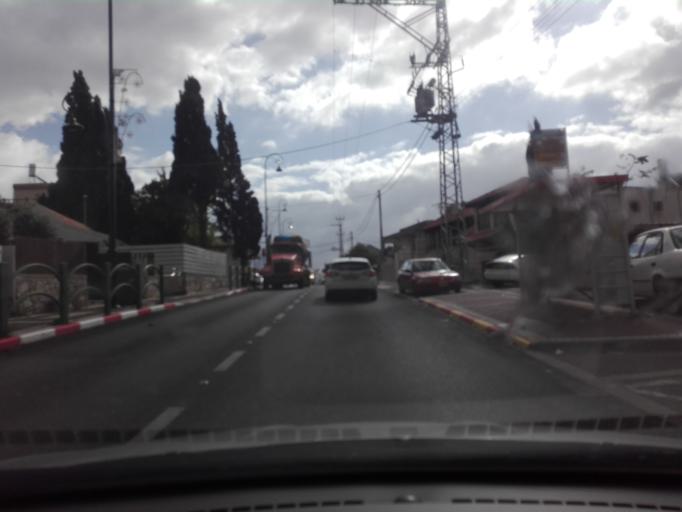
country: IL
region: Haifa
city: Daliyat el Karmil
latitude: 32.7205
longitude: 35.0622
